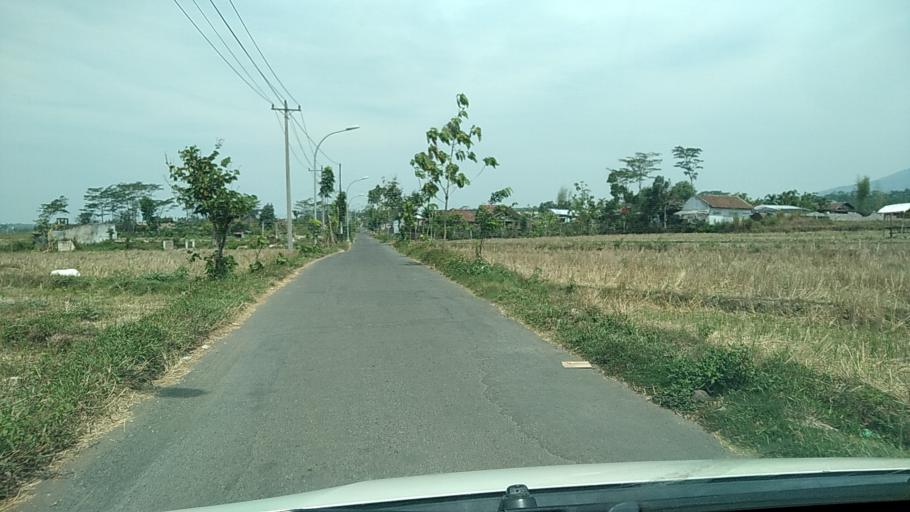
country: ID
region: Central Java
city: Ungaran
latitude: -7.0783
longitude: 110.3218
